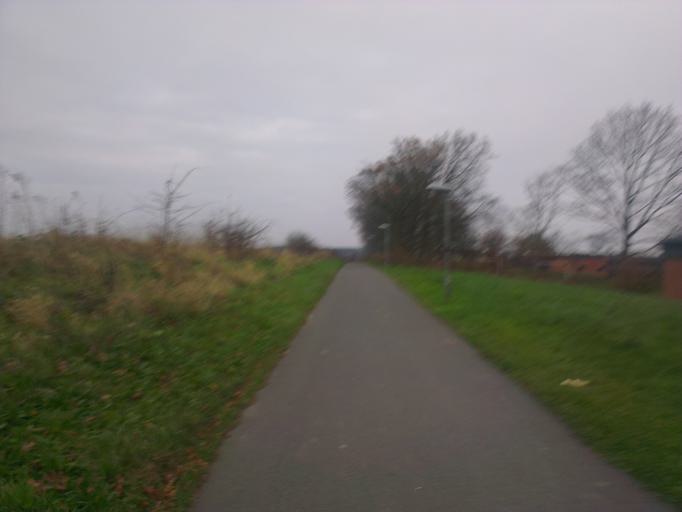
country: DK
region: Capital Region
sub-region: Frederikssund Kommune
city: Jaegerspris
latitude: 55.8446
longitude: 11.9856
